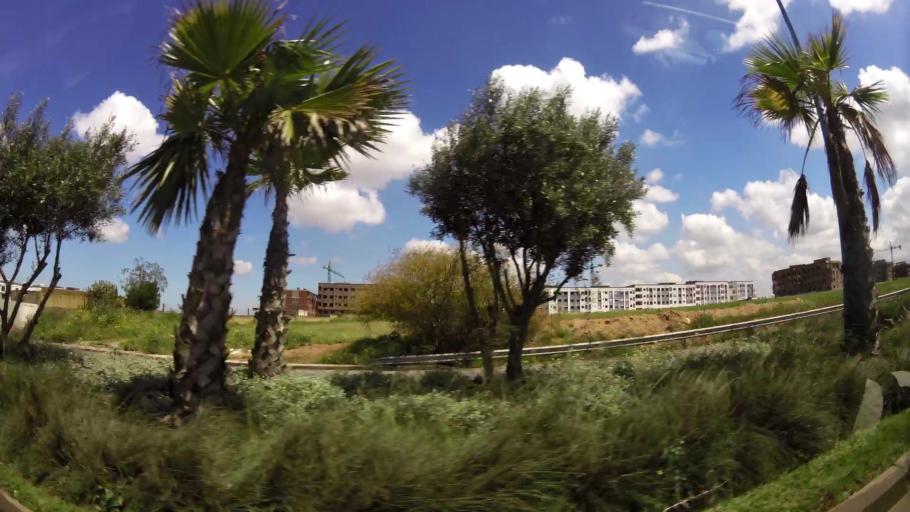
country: MA
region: Grand Casablanca
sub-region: Casablanca
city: Casablanca
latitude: 33.5214
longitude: -7.6164
